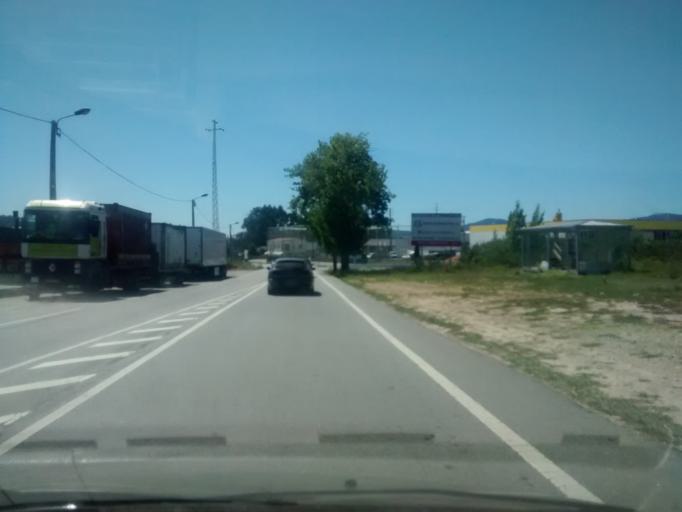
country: PT
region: Braga
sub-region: Barcelos
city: Galegos
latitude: 41.5210
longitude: -8.5732
